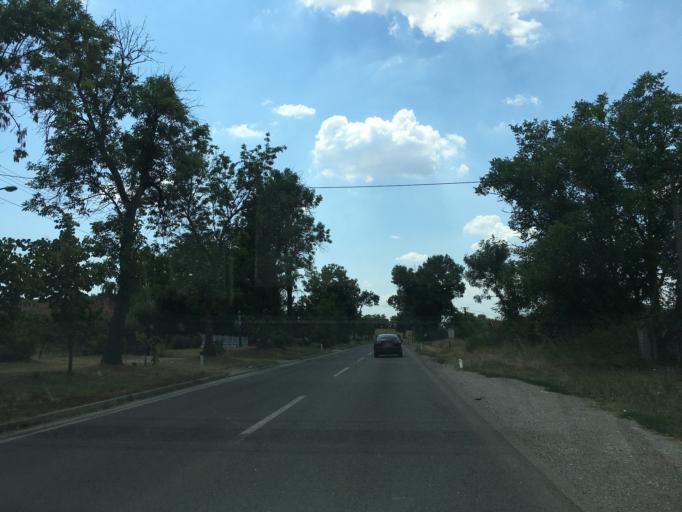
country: RS
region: Central Serbia
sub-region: Belgrade
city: Mladenovac
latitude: 44.4659
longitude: 20.6676
